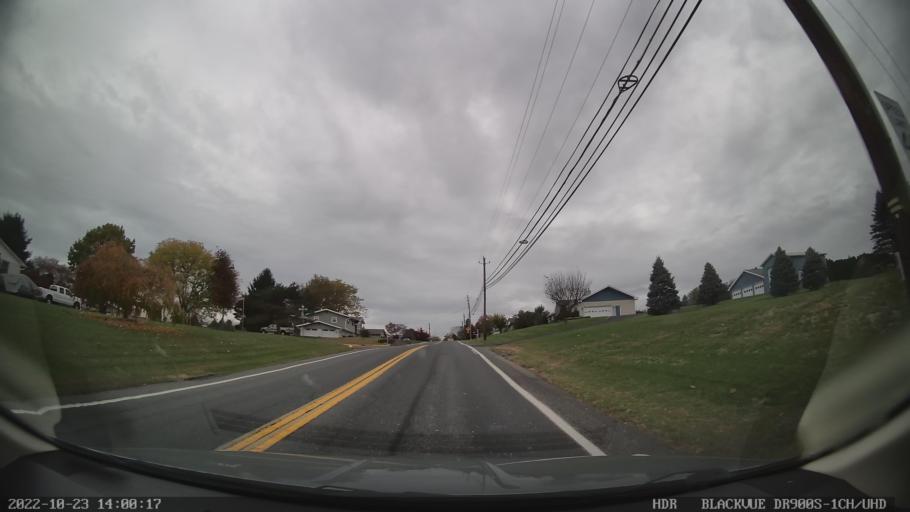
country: US
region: Pennsylvania
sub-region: Northampton County
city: Northampton
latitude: 40.7143
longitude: -75.4830
